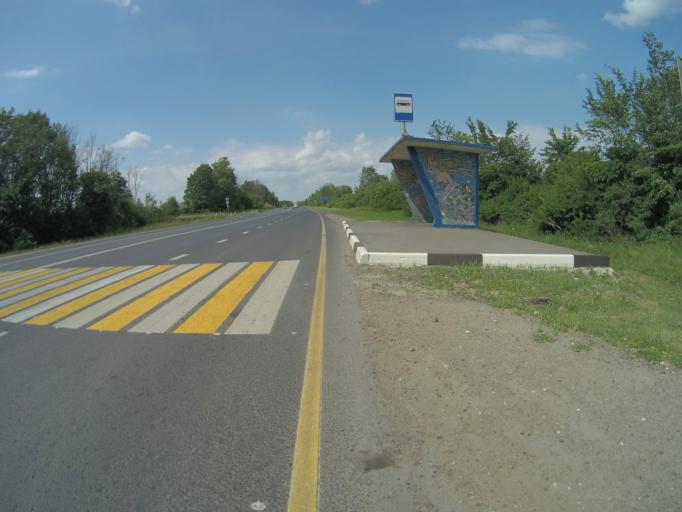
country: RU
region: Vladimir
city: Suzdal'
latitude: 56.3755
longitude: 40.4605
